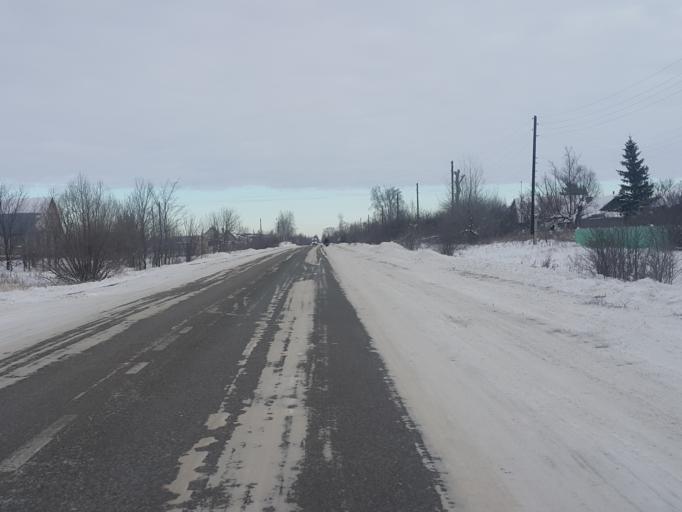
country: RU
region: Tambov
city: Platonovka
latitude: 52.8606
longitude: 41.8405
